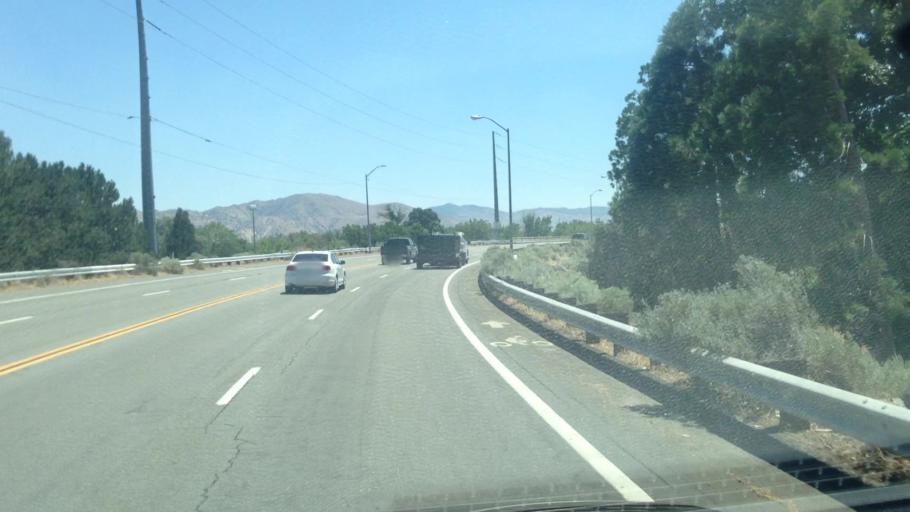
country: US
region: Nevada
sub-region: Washoe County
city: Sparks
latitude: 39.5200
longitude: -119.7622
